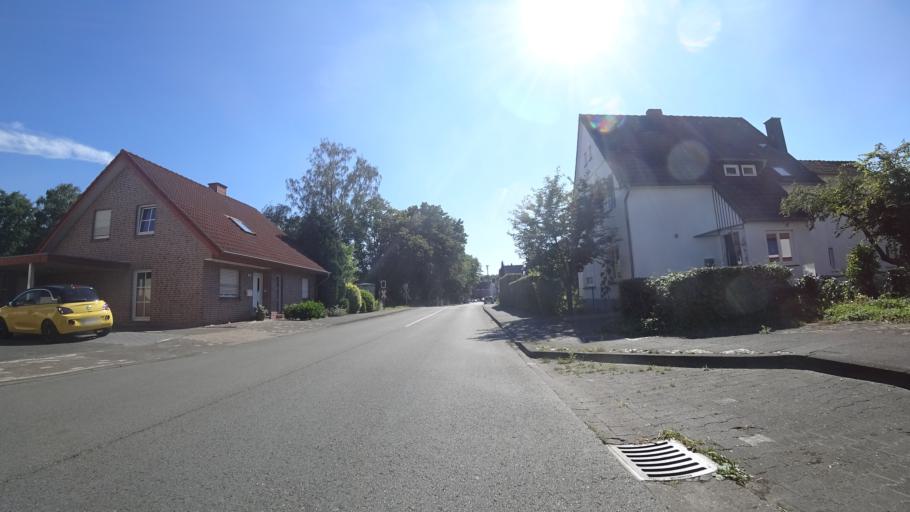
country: DE
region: North Rhine-Westphalia
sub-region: Regierungsbezirk Detmold
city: Guetersloh
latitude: 51.9188
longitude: 8.3884
